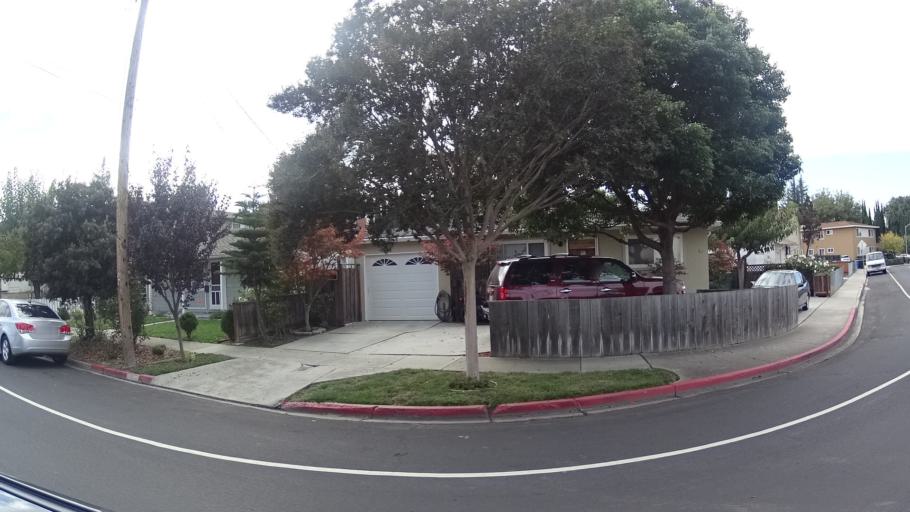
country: US
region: California
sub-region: Santa Clara County
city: Santa Clara
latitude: 37.3596
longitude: -121.9514
